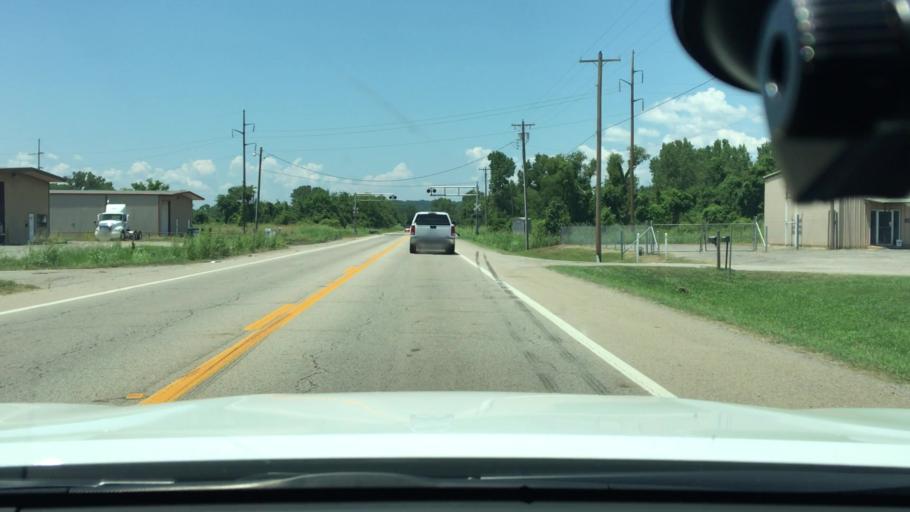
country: US
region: Arkansas
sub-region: Crawford County
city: Van Buren
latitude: 35.4176
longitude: -94.3341
